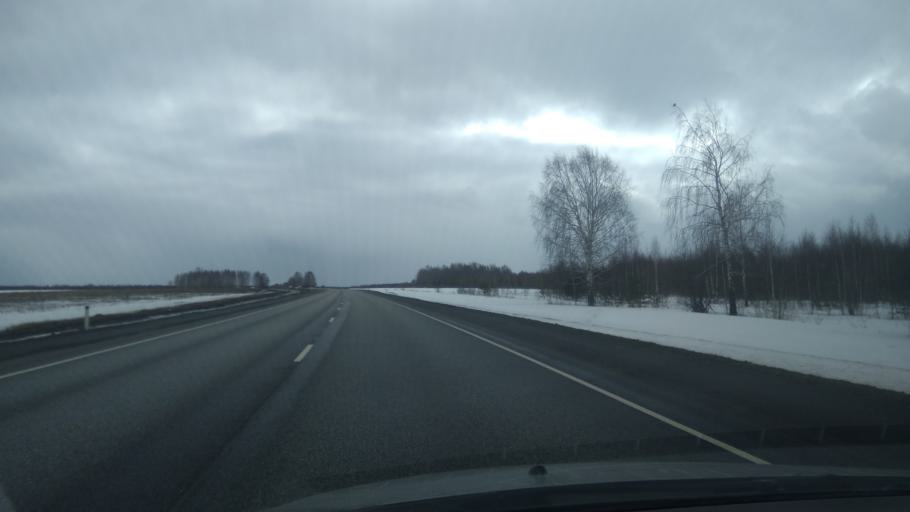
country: RU
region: Perm
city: Suksun
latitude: 56.9412
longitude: 57.5347
